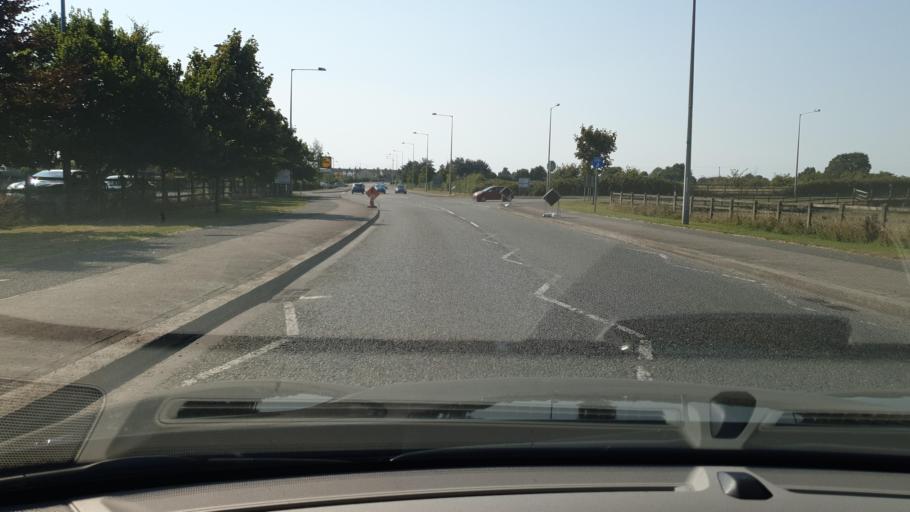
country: IE
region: Leinster
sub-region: An Mhi
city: Trim
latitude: 53.5622
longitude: -6.7887
